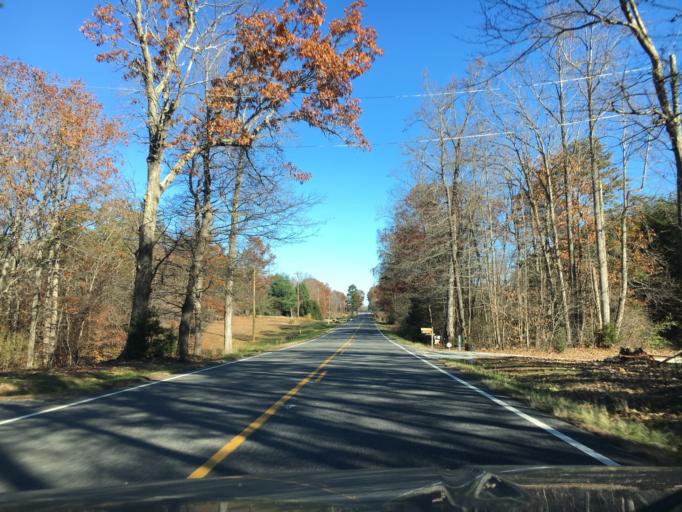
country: US
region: Virginia
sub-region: Appomattox County
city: Appomattox
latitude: 37.4428
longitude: -78.7185
